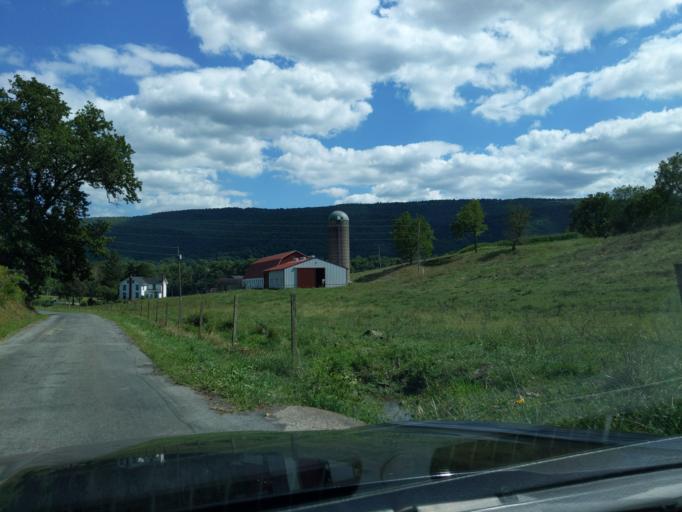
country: US
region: Pennsylvania
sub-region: Blair County
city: Tyrone
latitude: 40.6042
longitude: -78.2269
